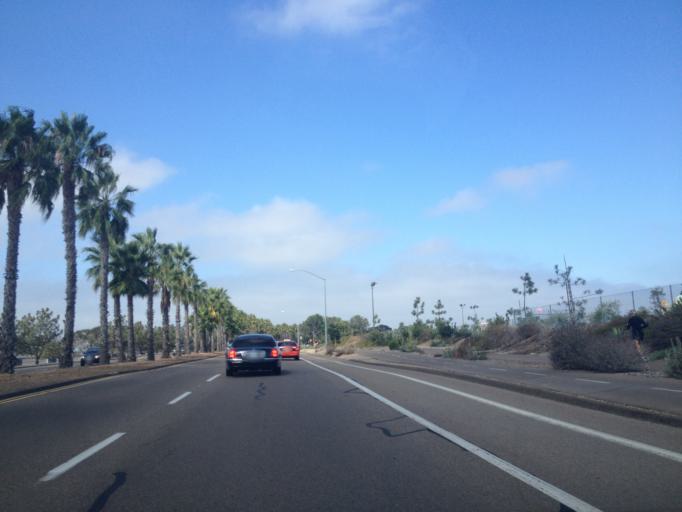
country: US
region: California
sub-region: San Diego County
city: San Diego
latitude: 32.7614
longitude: -117.2182
